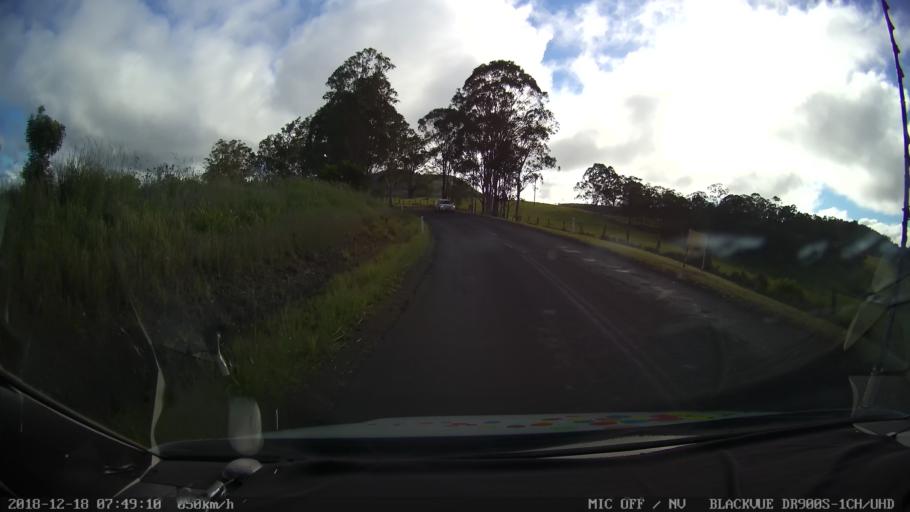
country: AU
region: New South Wales
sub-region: Kyogle
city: Kyogle
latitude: -28.4557
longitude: 152.5690
